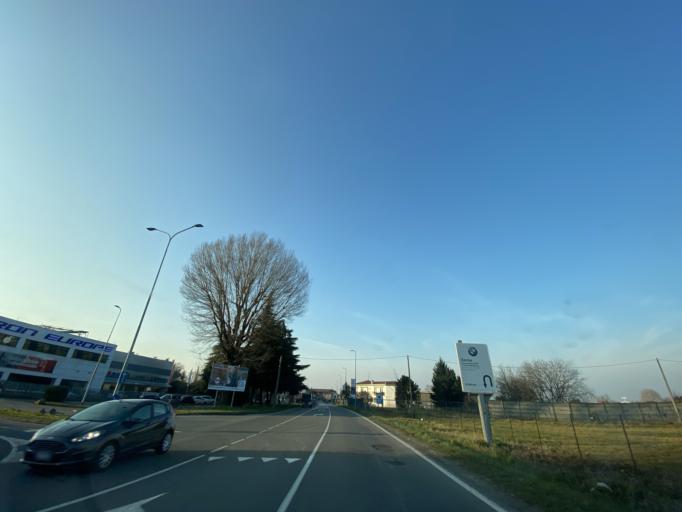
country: IT
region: Lombardy
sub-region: Citta metropolitana di Milano
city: Passirana
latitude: 45.5465
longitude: 9.0322
